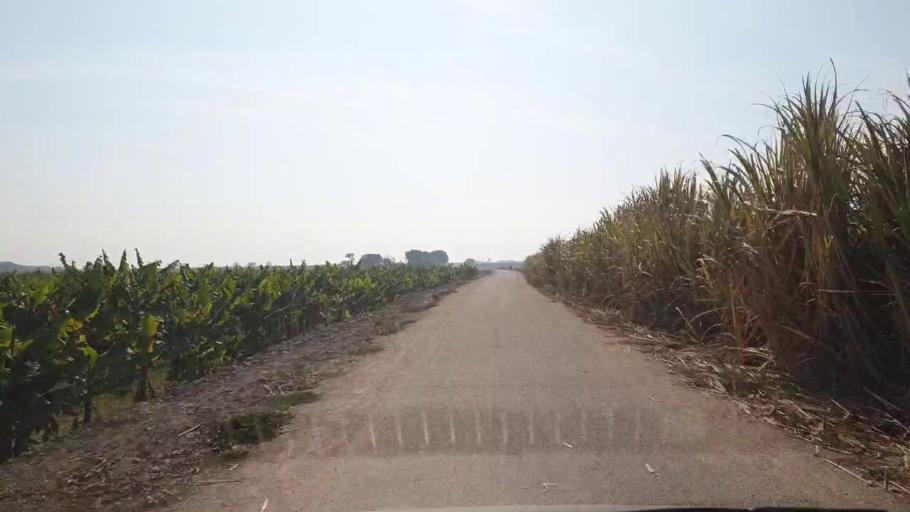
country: PK
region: Sindh
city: Tando Allahyar
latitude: 25.4034
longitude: 68.7398
